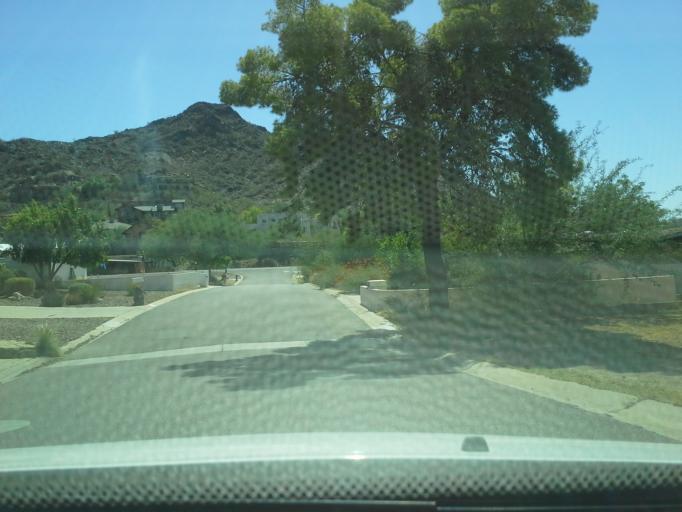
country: US
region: Arizona
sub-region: Maricopa County
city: Paradise Valley
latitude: 33.5725
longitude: -112.0463
